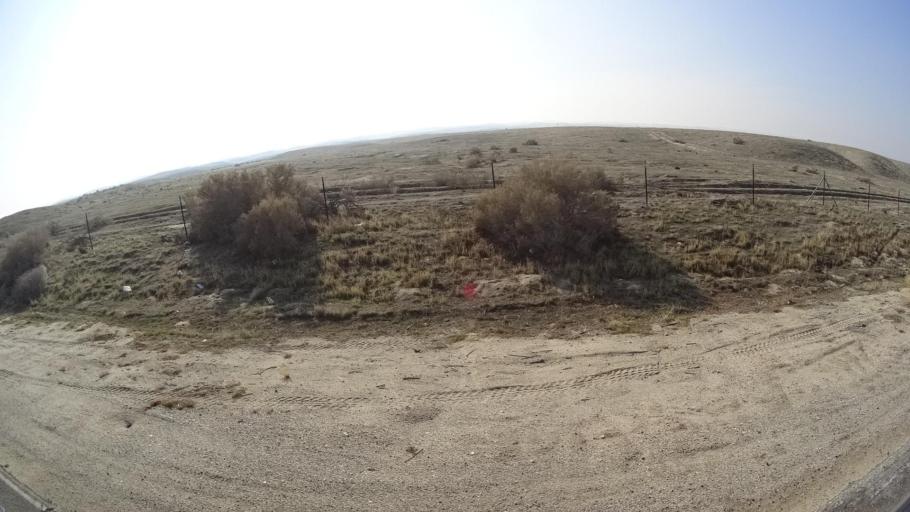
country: US
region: California
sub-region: Kern County
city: Buttonwillow
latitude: 35.3031
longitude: -119.3643
